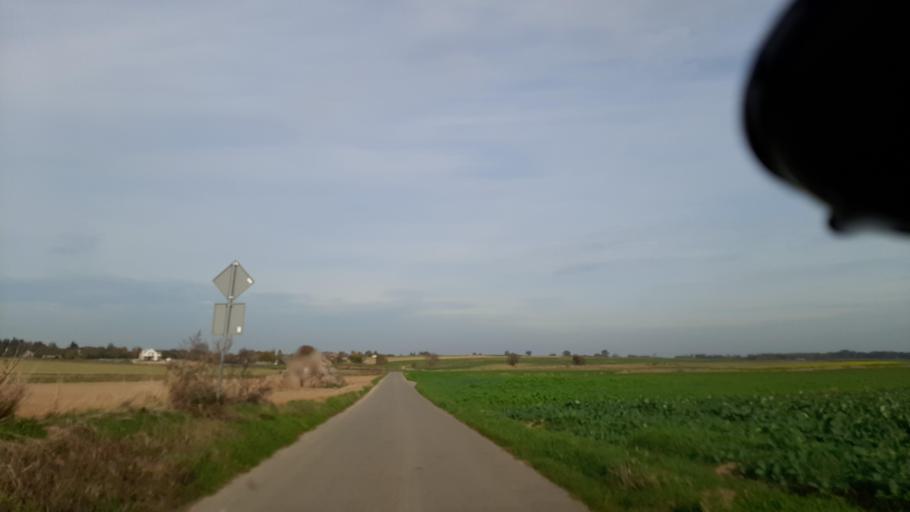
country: PL
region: Lublin Voivodeship
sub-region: Powiat lubelski
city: Jastkow
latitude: 51.3279
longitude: 22.4071
